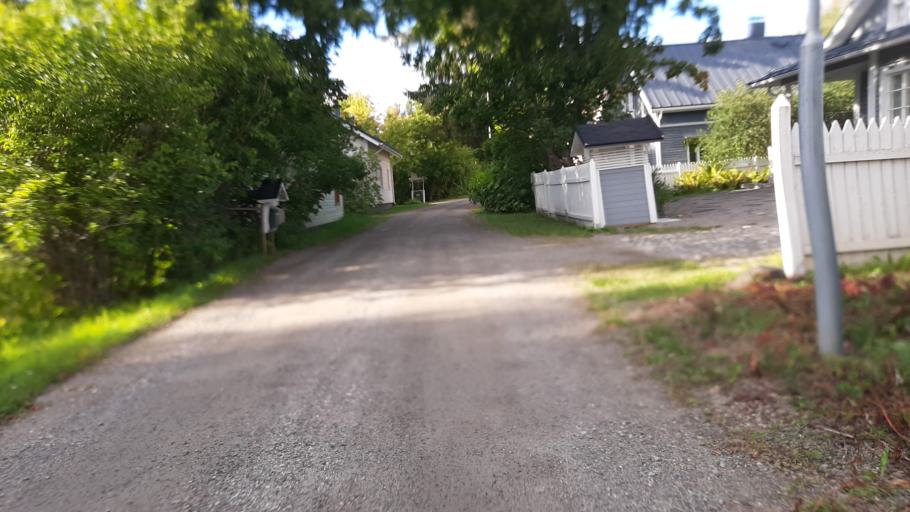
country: FI
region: North Karelia
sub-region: Joensuu
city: Joensuu
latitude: 62.6020
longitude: 29.8002
